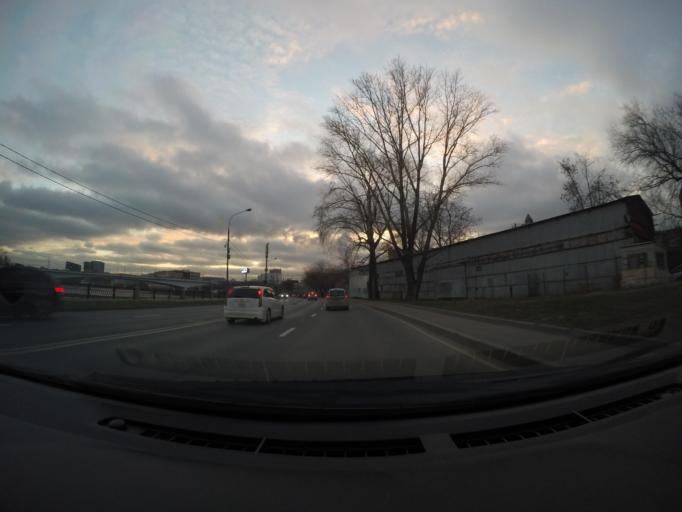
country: RU
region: Moscow
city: Zamoskvorech'ye
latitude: 55.7082
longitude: 37.6305
